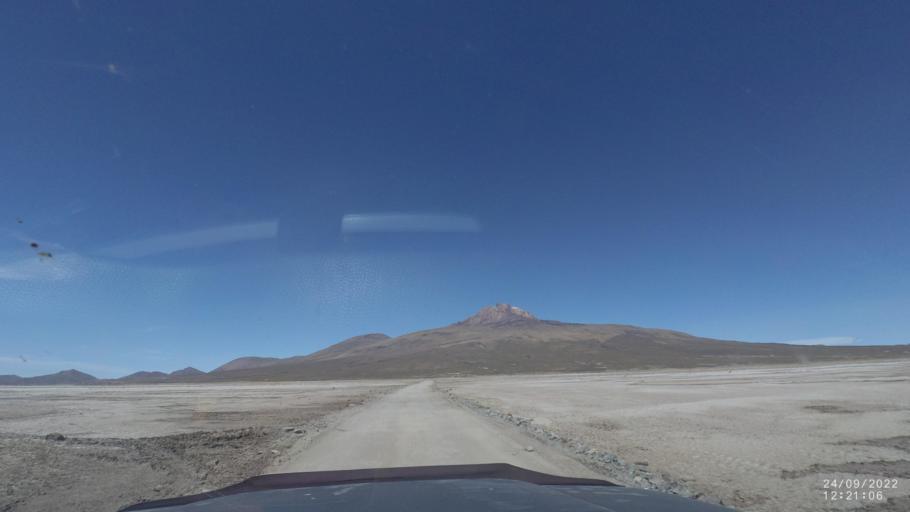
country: BO
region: Potosi
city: Colchani
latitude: -19.7464
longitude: -67.6701
